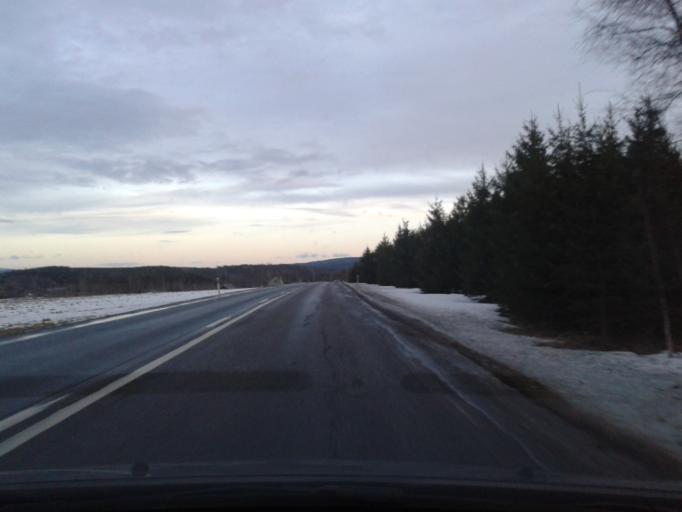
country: SE
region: Vaesternorrland
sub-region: Solleftea Kommun
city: Solleftea
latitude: 63.1488
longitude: 17.3714
